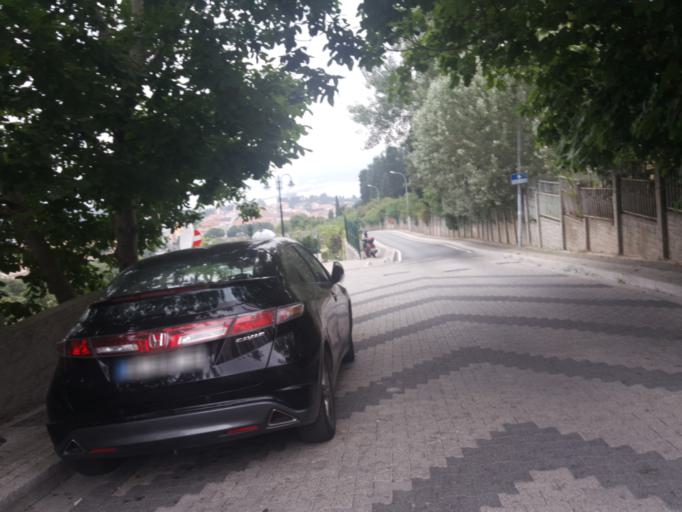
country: TR
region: Istanbul
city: UEskuedar
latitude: 41.0388
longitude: 29.0586
